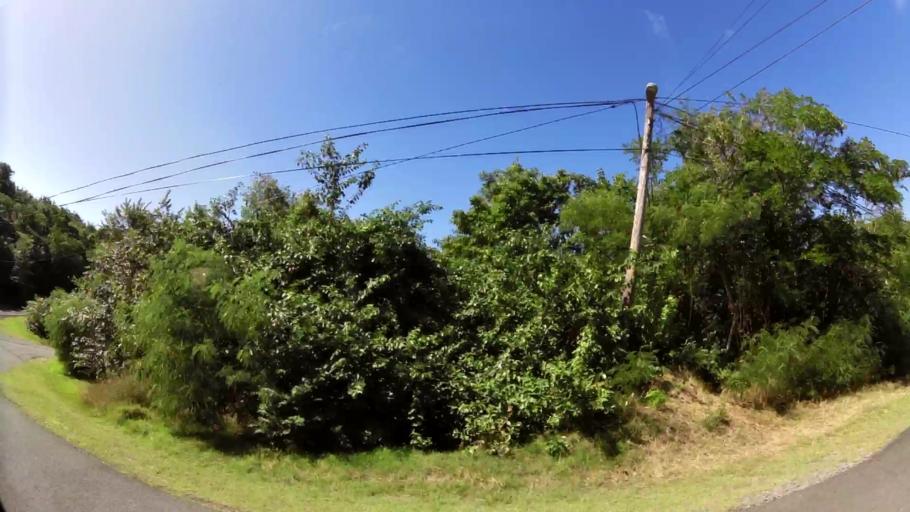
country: LC
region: Vieux-Fort
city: Vieux Fort
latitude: 13.7209
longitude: -60.9499
